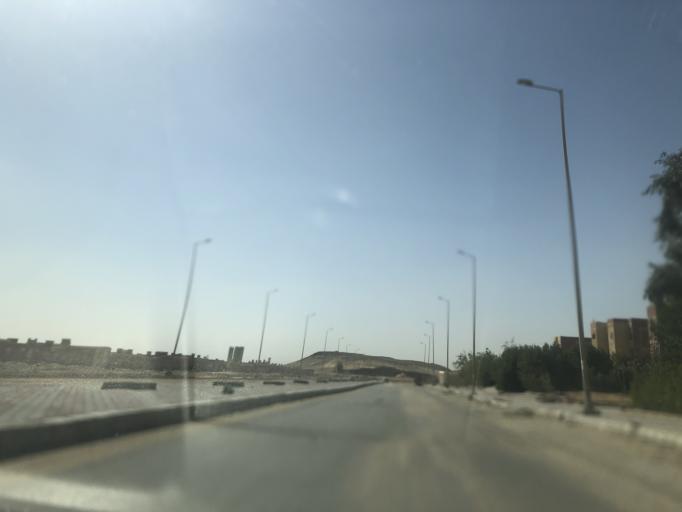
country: EG
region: Al Jizah
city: Madinat Sittah Uktubar
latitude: 29.9327
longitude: 30.9594
